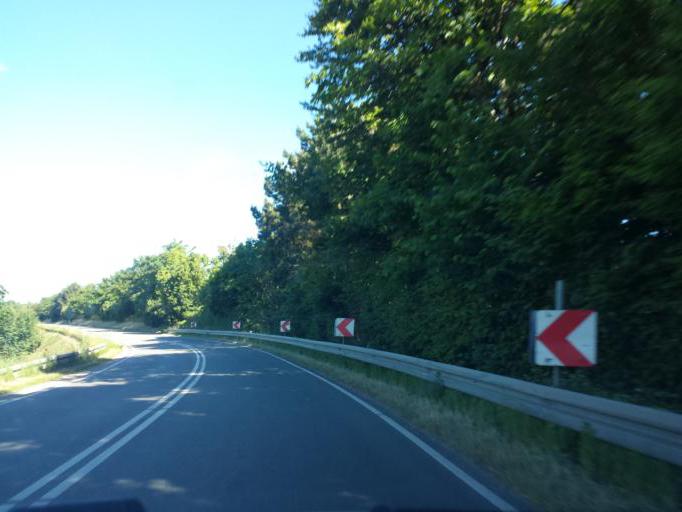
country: DK
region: Capital Region
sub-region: Egedal Kommune
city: Ganlose
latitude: 55.7779
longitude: 12.2912
